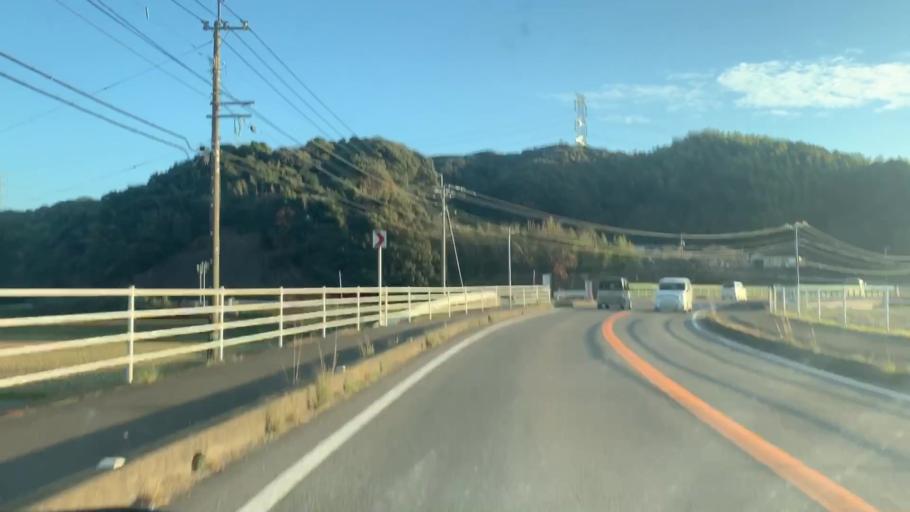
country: JP
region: Saga Prefecture
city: Karatsu
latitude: 33.3628
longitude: 130.0097
